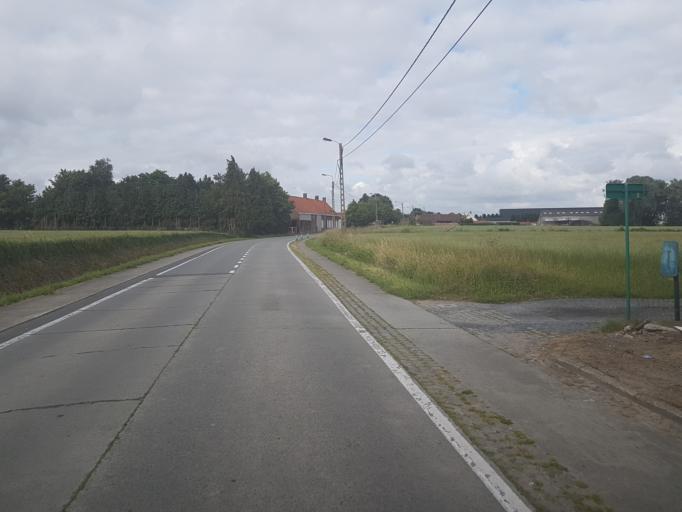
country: BE
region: Flanders
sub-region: Provincie West-Vlaanderen
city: Anzegem
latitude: 50.8450
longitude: 3.4348
